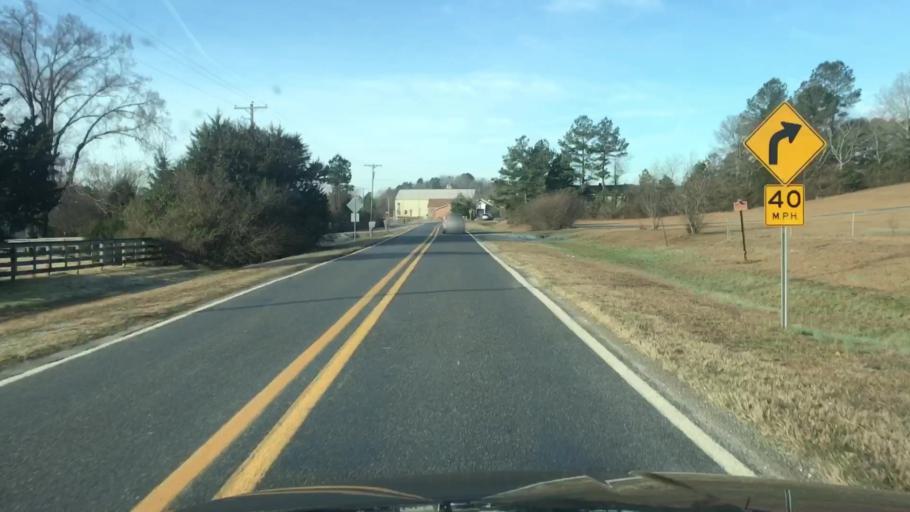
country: US
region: Arkansas
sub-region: Garland County
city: Rockwell
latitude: 34.4716
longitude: -93.2443
